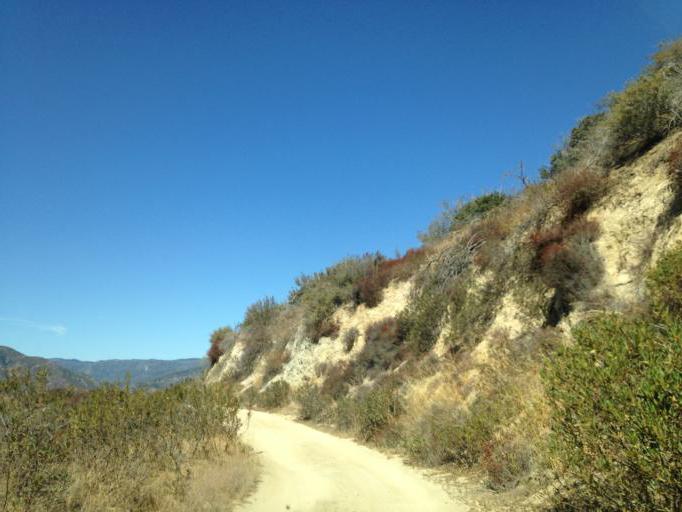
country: US
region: California
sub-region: San Bernardino County
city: Mentone
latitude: 34.1257
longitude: -117.1098
